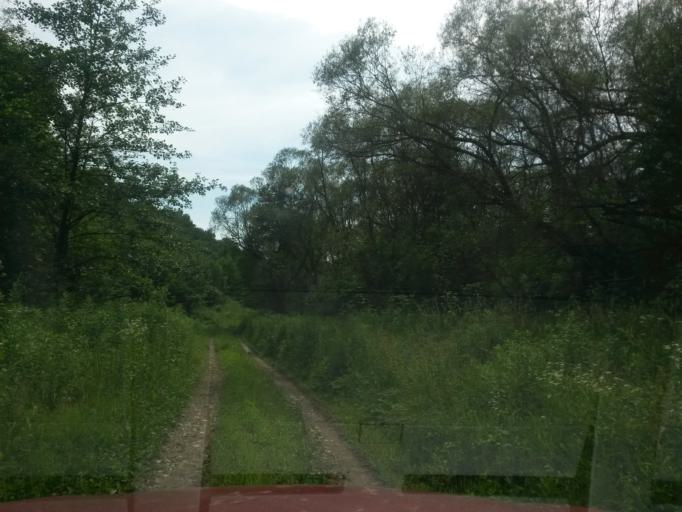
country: SK
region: Kosicky
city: Moldava nad Bodvou
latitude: 48.6498
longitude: 21.1068
